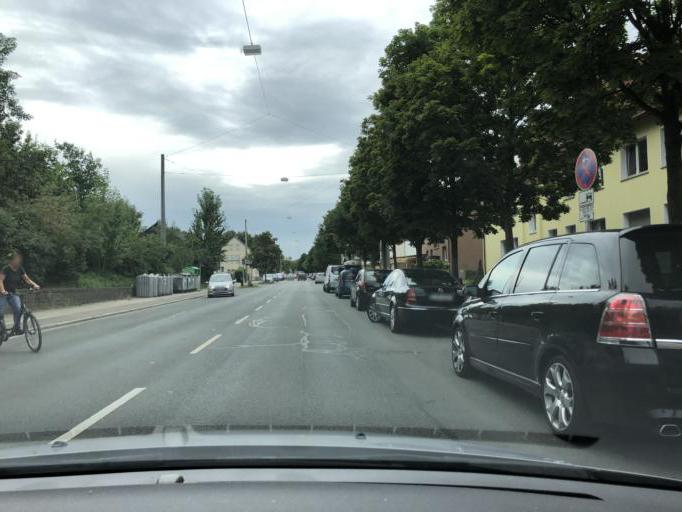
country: DE
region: North Rhine-Westphalia
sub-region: Regierungsbezirk Munster
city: Bottrop
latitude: 51.4853
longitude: 6.9500
